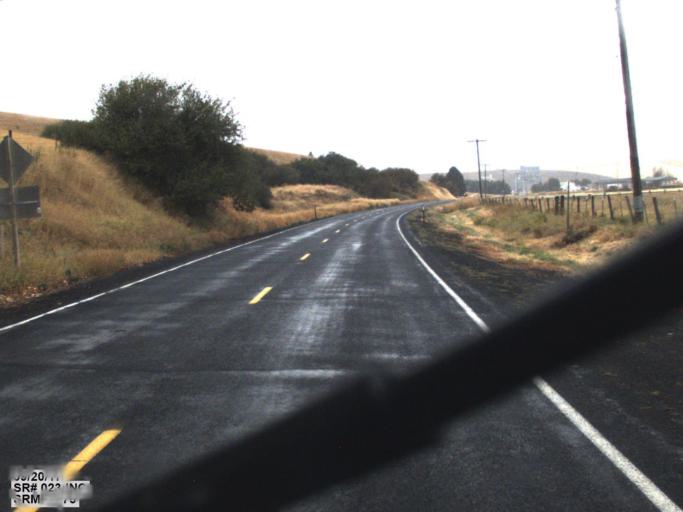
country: US
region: Washington
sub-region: Whitman County
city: Colfax
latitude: 47.0101
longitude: -117.4701
